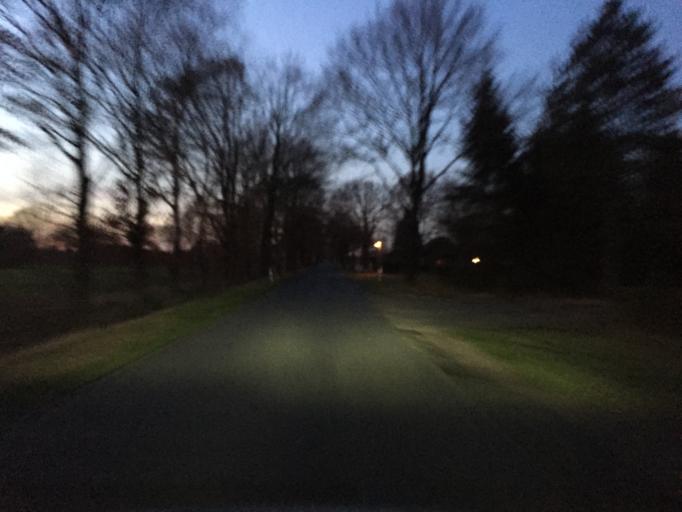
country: DE
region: Lower Saxony
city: Barenburg
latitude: 52.6420
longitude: 8.8333
